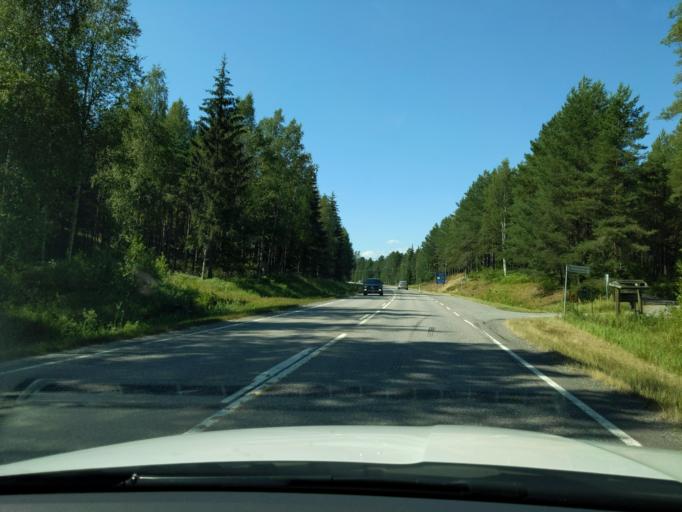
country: FI
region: Uusimaa
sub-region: Raaseporin
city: Ekenaes
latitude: 60.0139
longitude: 23.3934
